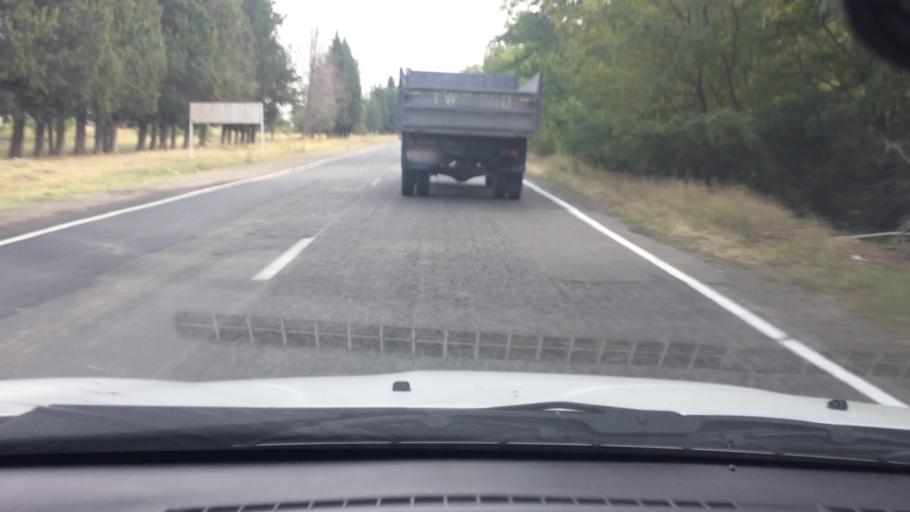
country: GE
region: Kvemo Kartli
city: Rust'avi
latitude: 41.4657
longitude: 44.9828
